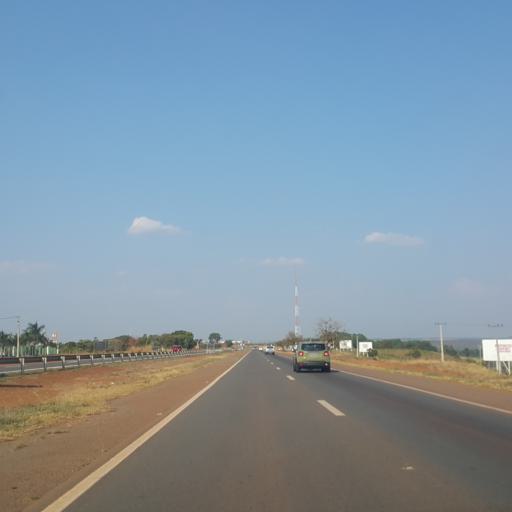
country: BR
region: Goias
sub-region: Abadiania
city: Abadiania
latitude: -16.1215
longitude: -48.4237
